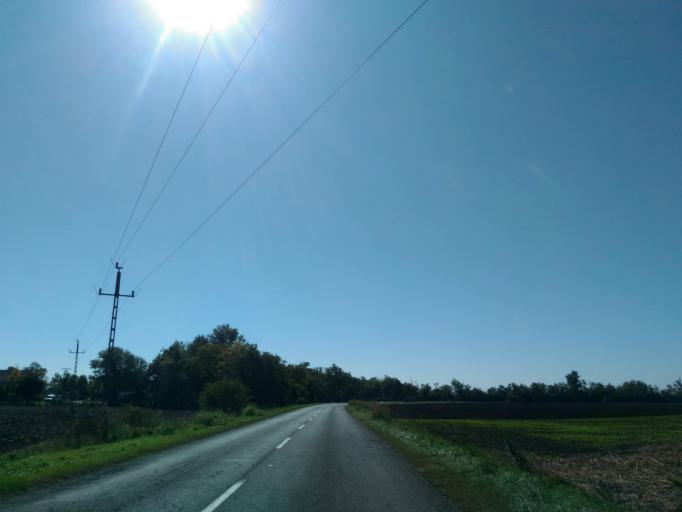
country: HU
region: Fejer
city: Ivancsa
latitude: 47.1693
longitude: 18.7949
